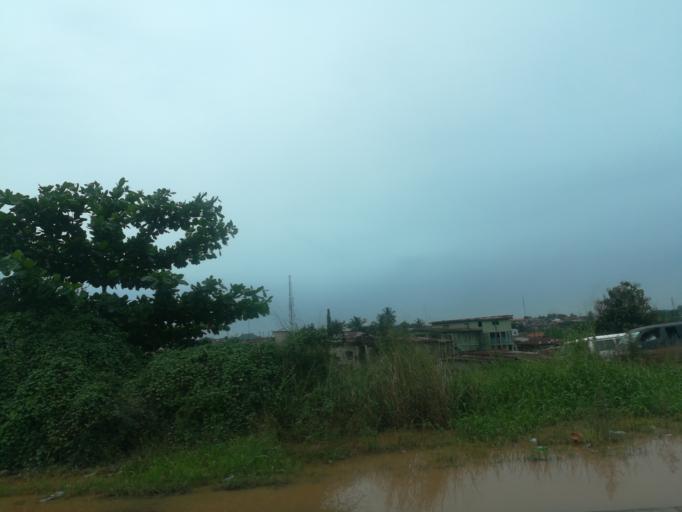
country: NG
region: Oyo
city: Ibadan
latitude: 7.3839
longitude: 3.9346
